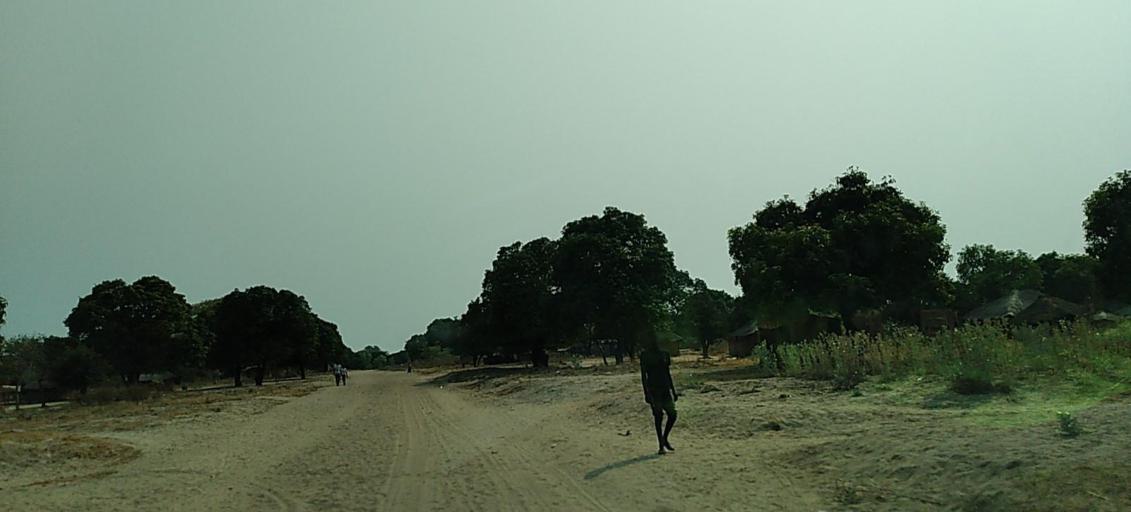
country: ZM
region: North-Western
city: Zambezi
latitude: -13.1718
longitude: 23.4036
